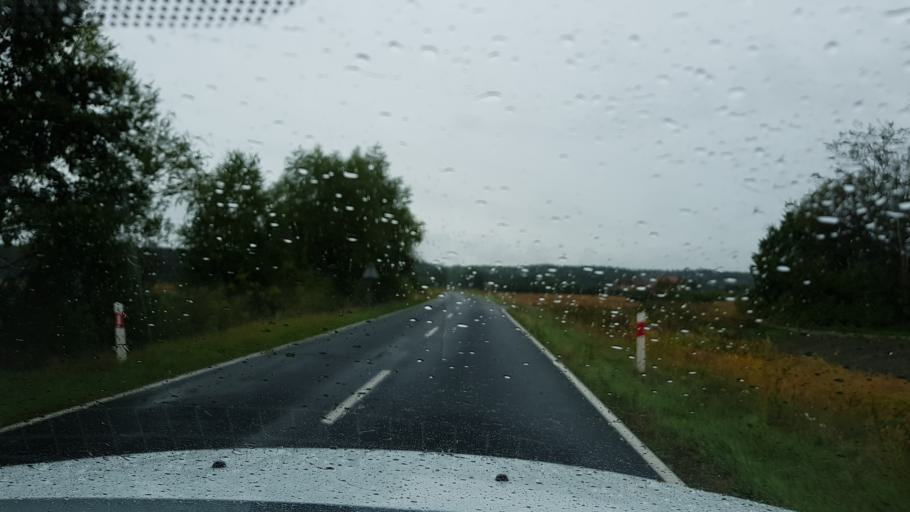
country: PL
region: West Pomeranian Voivodeship
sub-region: Powiat gryfinski
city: Widuchowa
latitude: 53.0790
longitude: 14.3751
